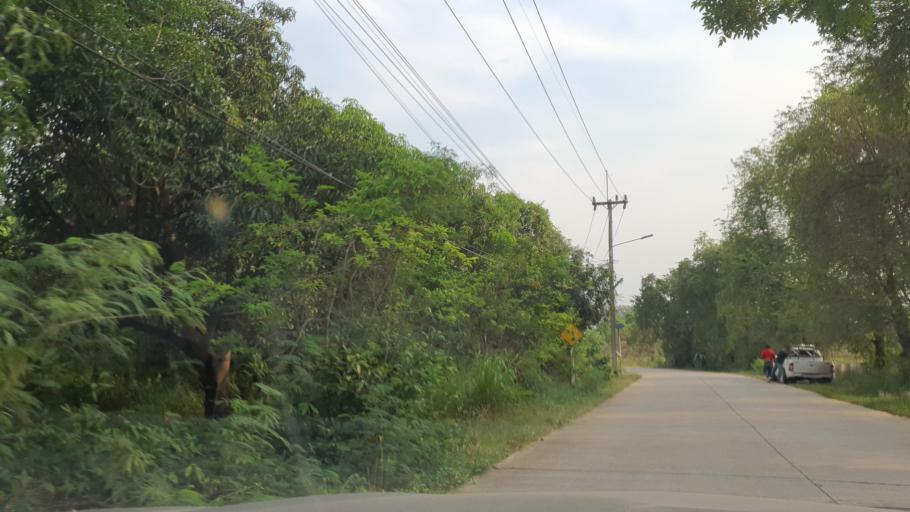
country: TH
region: Rayong
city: Rayong
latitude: 12.6061
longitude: 101.3996
